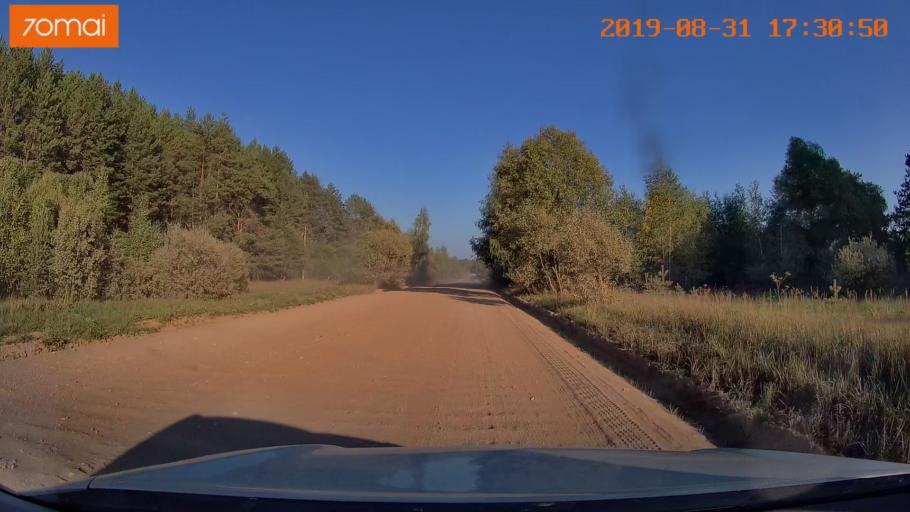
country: RU
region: Kaluga
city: Detchino
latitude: 54.8099
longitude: 36.3391
